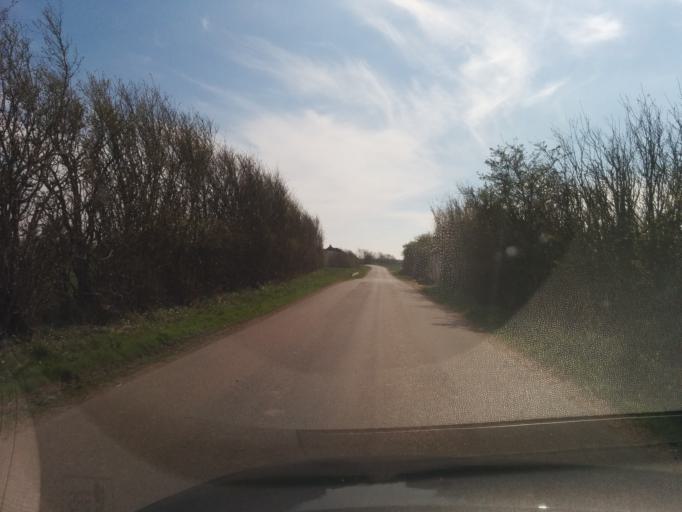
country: DK
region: South Denmark
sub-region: Kolding Kommune
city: Christiansfeld
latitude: 55.3880
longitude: 9.4014
